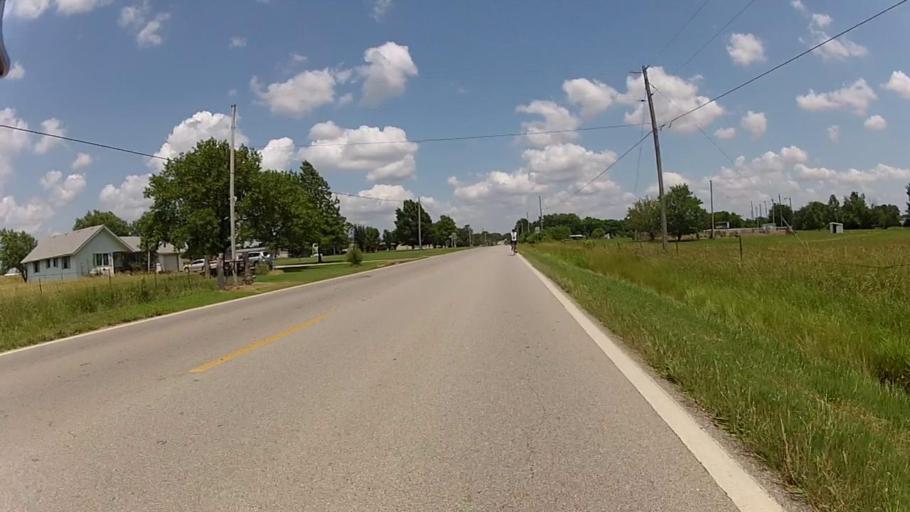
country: US
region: Kansas
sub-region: Labette County
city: Altamont
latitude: 37.1931
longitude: -95.3069
